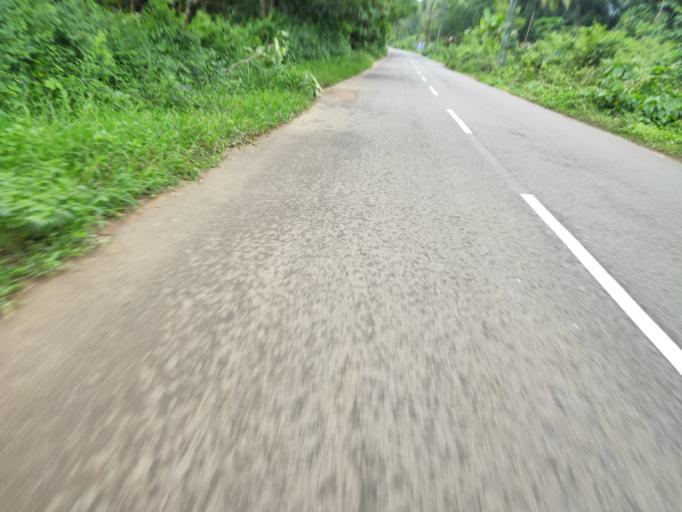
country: IN
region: Kerala
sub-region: Malappuram
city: Manjeri
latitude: 11.2250
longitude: 76.2675
